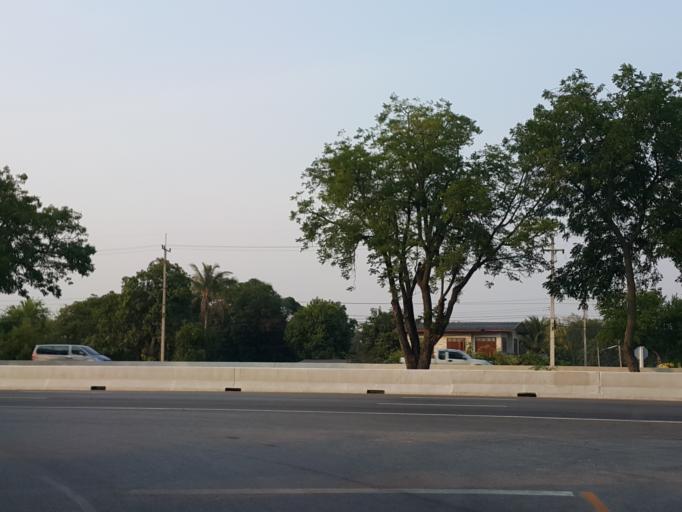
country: TH
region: Chai Nat
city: Sapphaya
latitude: 15.1173
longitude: 100.2741
